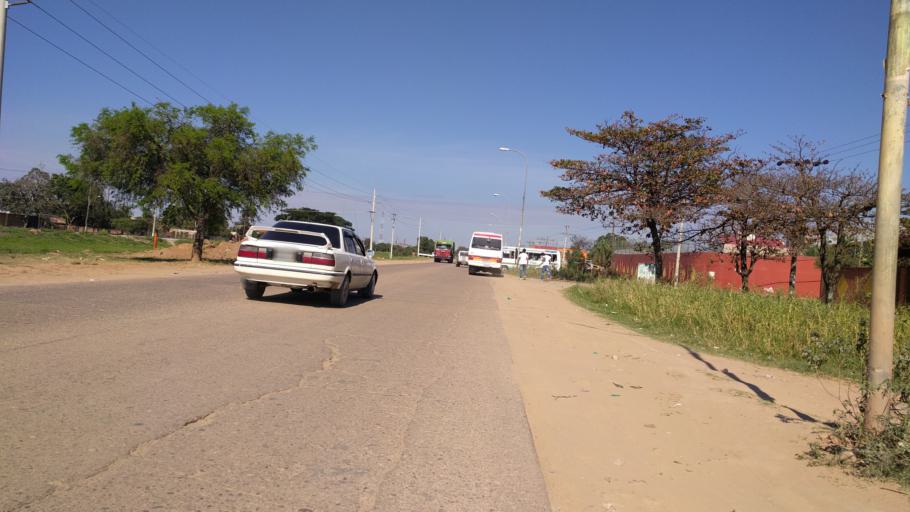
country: BO
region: Santa Cruz
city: Santa Cruz de la Sierra
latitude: -17.8570
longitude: -63.1858
